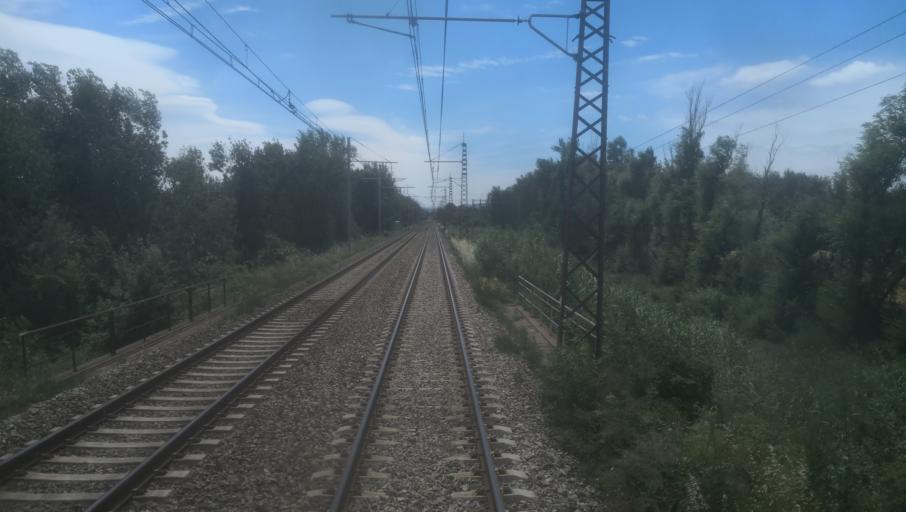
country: FR
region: Languedoc-Roussillon
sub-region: Departement de l'Aude
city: Narbonne
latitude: 43.2073
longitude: 3.0225
